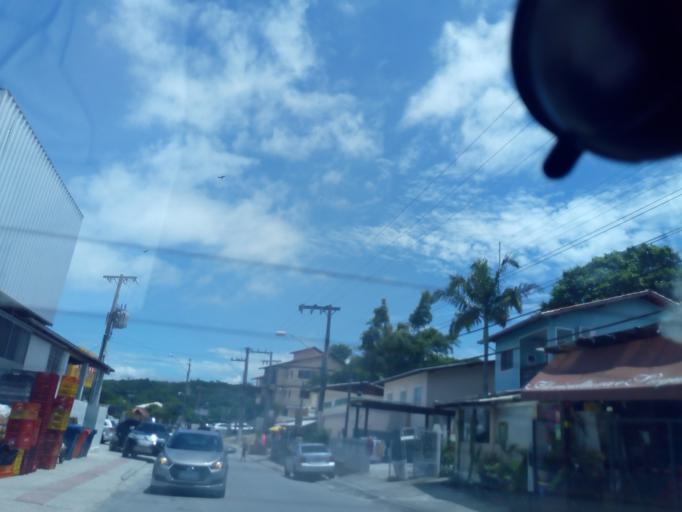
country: BR
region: Santa Catarina
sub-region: Florianopolis
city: Itacorubi
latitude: -27.3968
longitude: -48.4264
